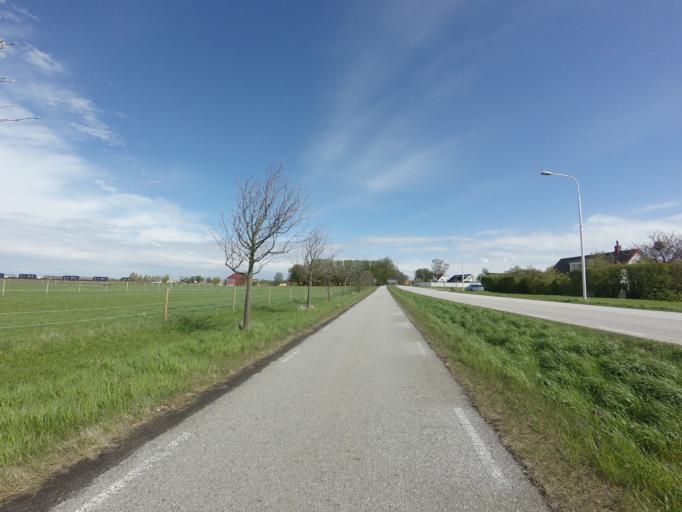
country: SE
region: Skane
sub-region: Malmo
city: Tygelsjo
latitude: 55.5115
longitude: 12.9950
